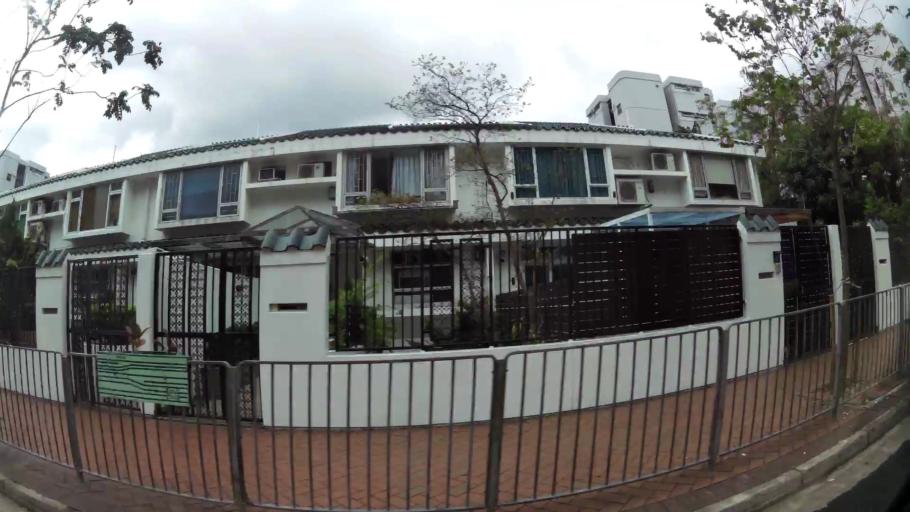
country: HK
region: Sham Shui Po
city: Sham Shui Po
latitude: 22.3338
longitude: 114.1755
